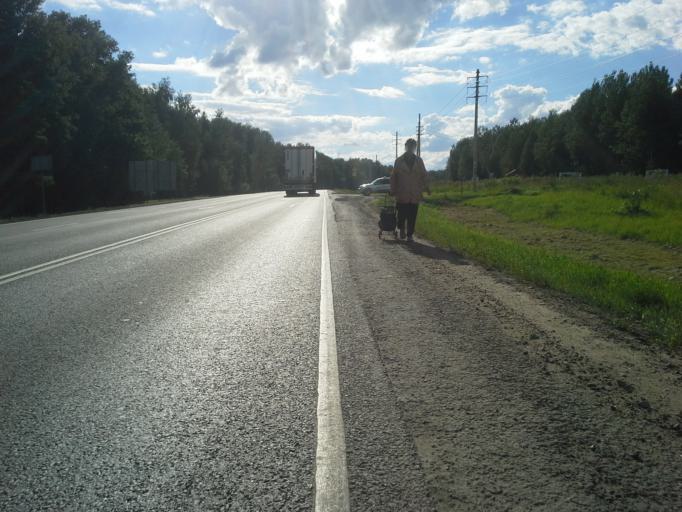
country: RU
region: Moskovskaya
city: L'vovskiy
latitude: 55.3341
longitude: 37.4825
